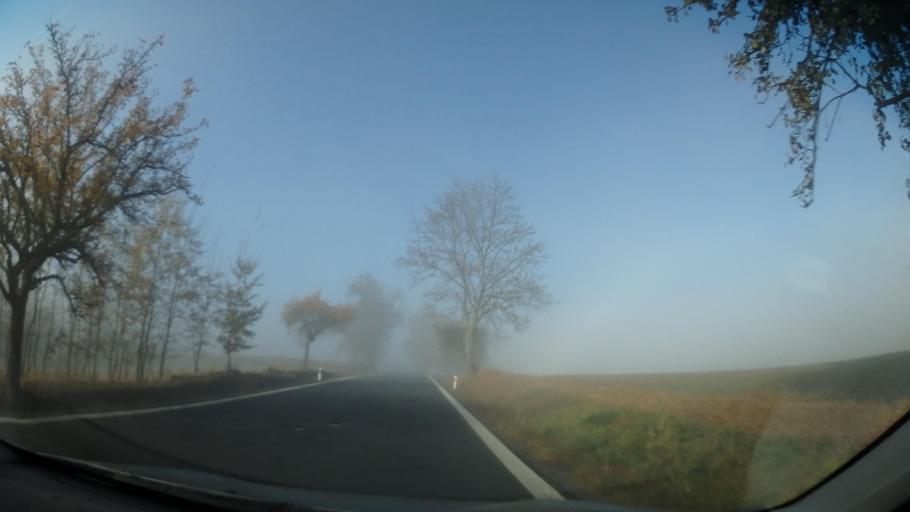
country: CZ
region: Vysocina
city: Krizanov
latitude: 49.4412
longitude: 16.1837
